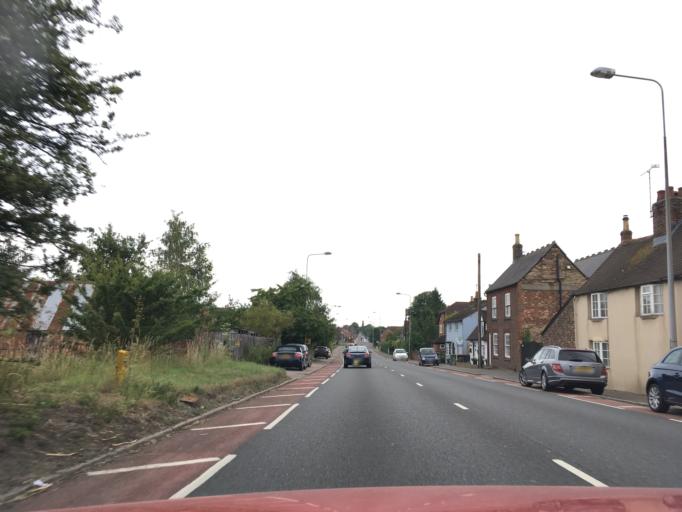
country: GB
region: England
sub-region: Central Bedfordshire
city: Hockliffe
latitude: 51.9335
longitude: -0.5901
